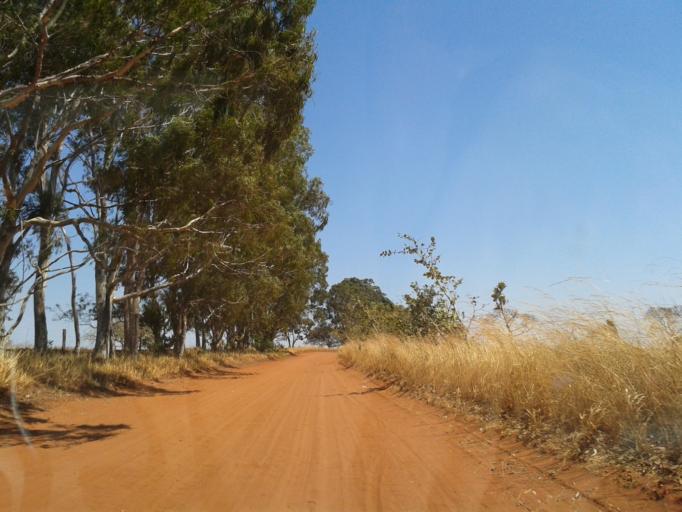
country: BR
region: Minas Gerais
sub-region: Ituiutaba
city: Ituiutaba
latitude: -18.9936
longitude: -49.3787
